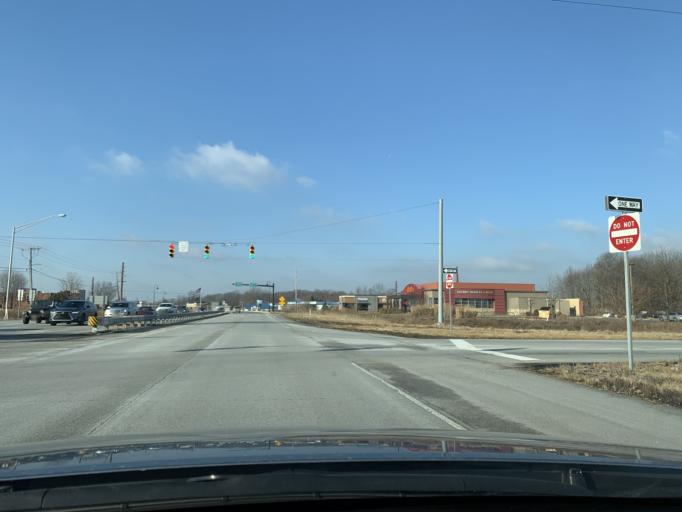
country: US
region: Indiana
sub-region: Porter County
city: Valparaiso
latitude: 41.4695
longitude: -87.0233
